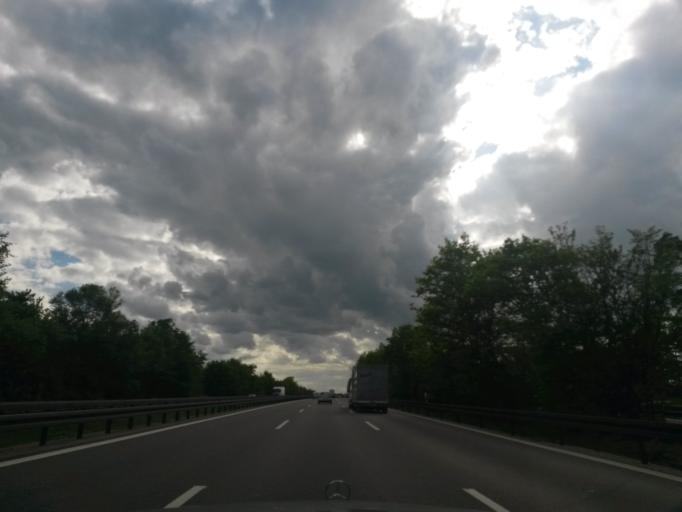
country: DE
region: Bavaria
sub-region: Regierungsbezirk Mittelfranken
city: Sachsen
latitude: 49.2658
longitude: 10.6942
